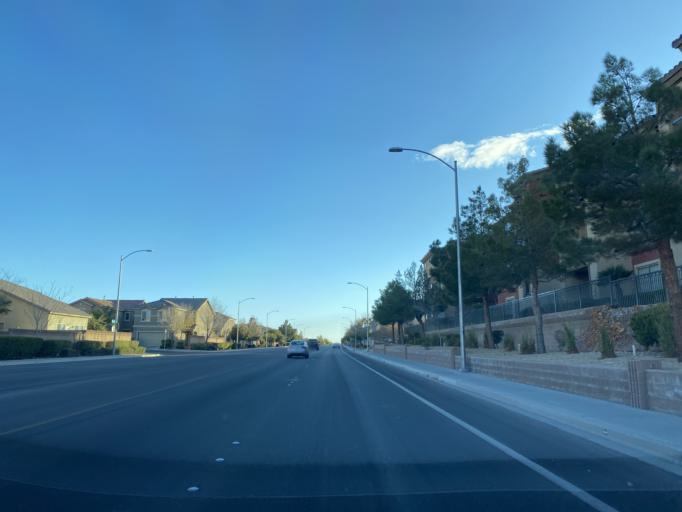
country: US
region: Nevada
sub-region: Clark County
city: Summerlin South
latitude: 36.3058
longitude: -115.3059
